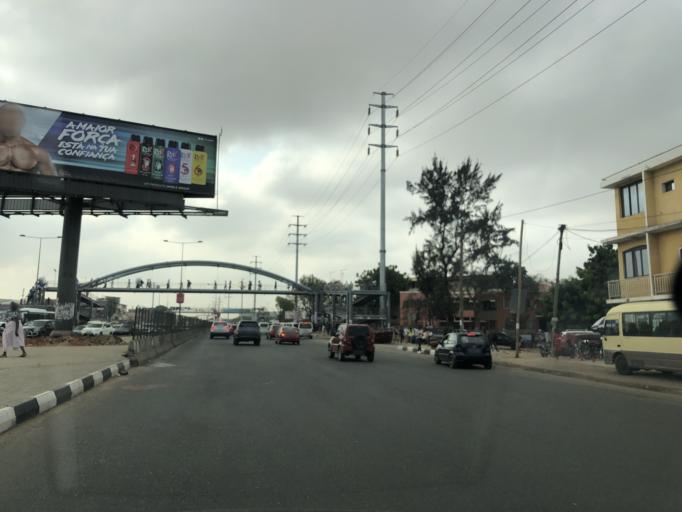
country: AO
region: Luanda
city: Luanda
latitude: -8.8364
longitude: 13.2593
